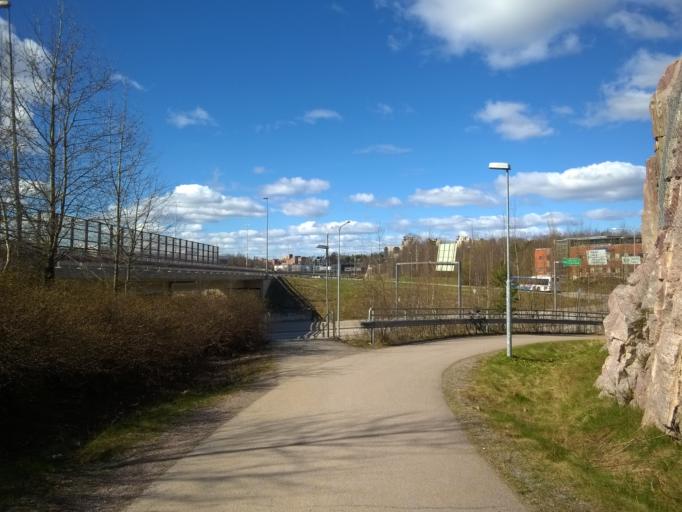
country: FI
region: Uusimaa
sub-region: Helsinki
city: Vantaa
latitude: 60.2292
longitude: 25.0122
